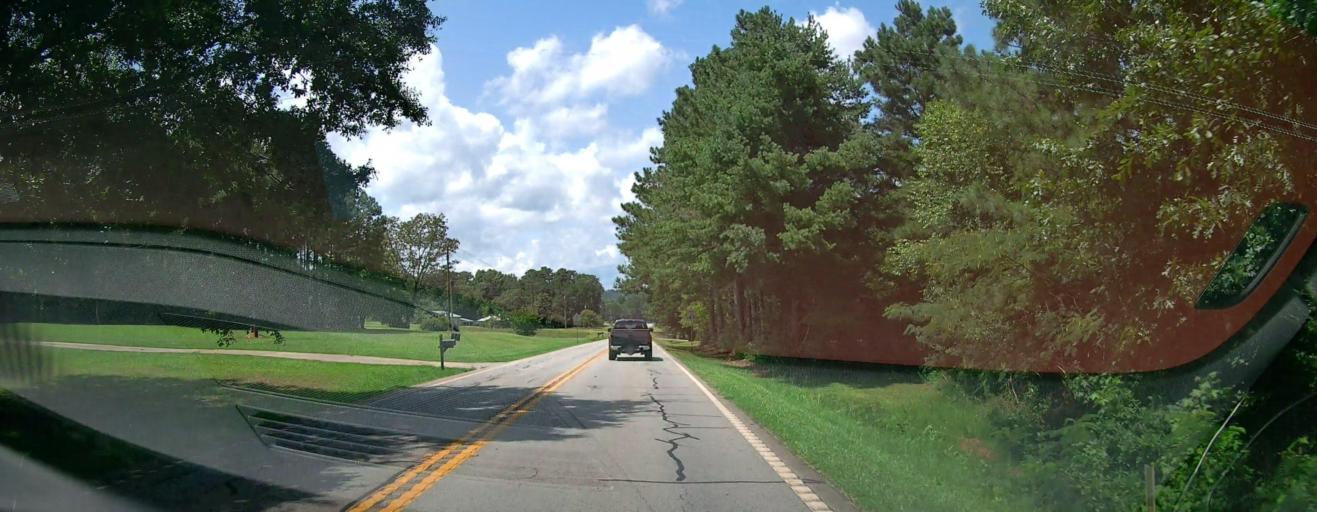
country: US
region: Georgia
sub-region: Carroll County
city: Bowdon
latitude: 33.4079
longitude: -85.2547
